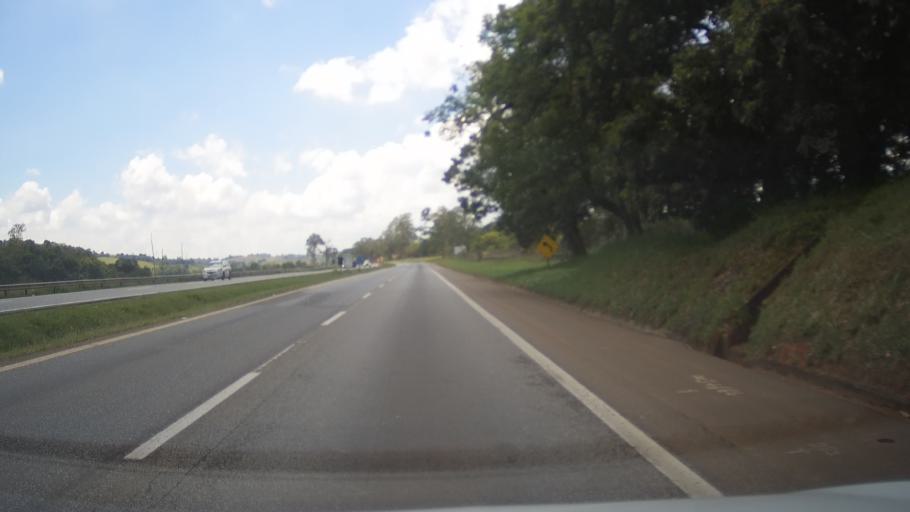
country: BR
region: Minas Gerais
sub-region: Sao Goncalo Do Sapucai
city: Sao Goncalo do Sapucai
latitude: -21.9196
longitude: -45.6007
